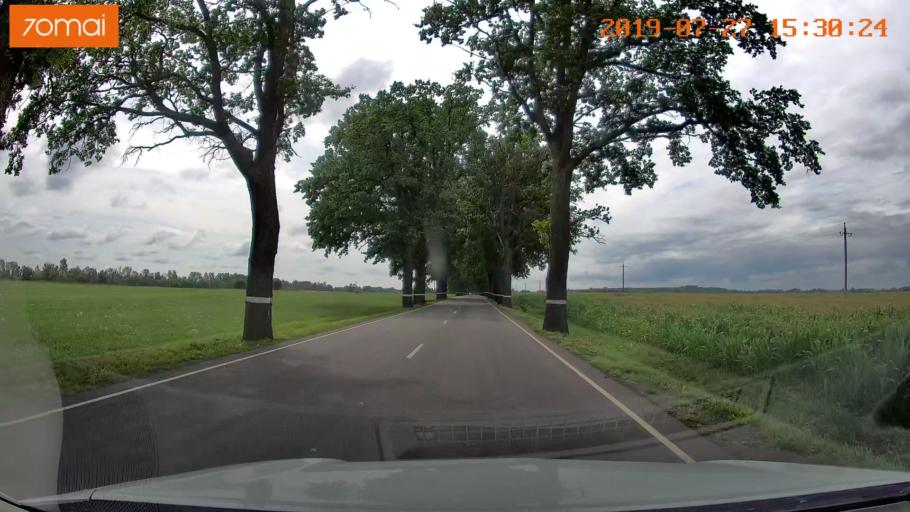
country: RU
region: Kaliningrad
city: Nesterov
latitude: 54.6279
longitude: 22.5126
